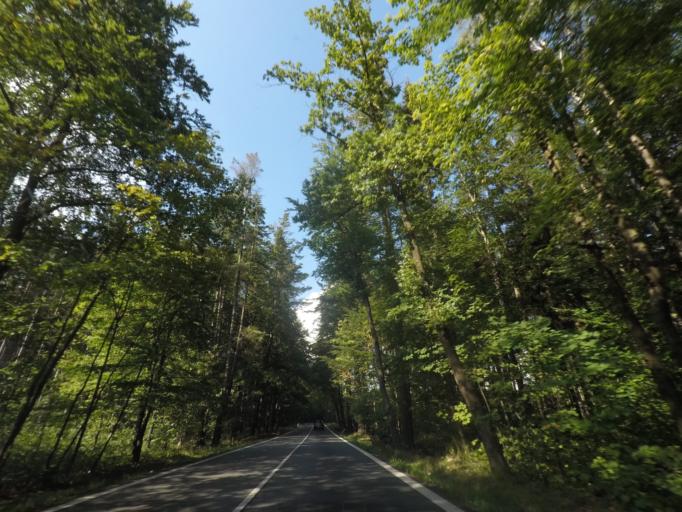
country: CZ
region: Kralovehradecky
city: Dvur Kralove nad Labem
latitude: 50.4652
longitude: 15.8656
